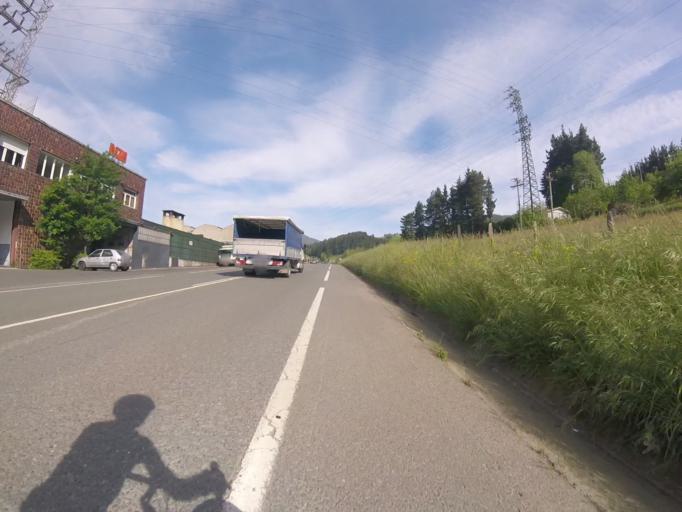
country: ES
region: Basque Country
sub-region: Provincia de Guipuzcoa
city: Zumarraga
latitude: 43.0781
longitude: -2.2936
